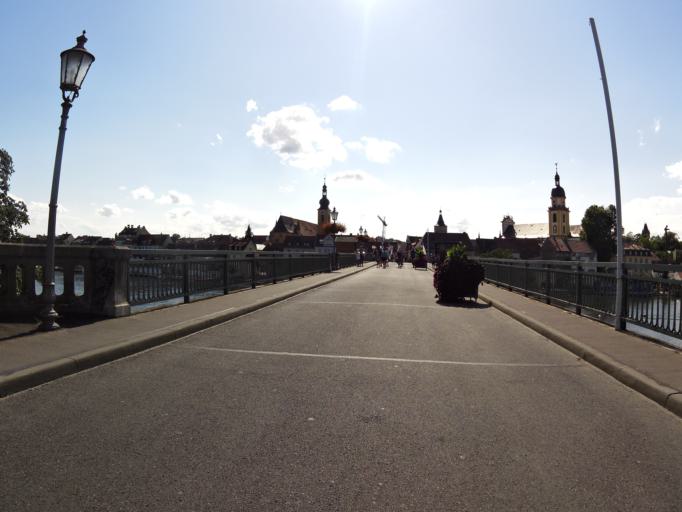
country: DE
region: Bavaria
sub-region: Regierungsbezirk Unterfranken
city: Kitzingen
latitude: 49.7406
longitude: 10.1658
